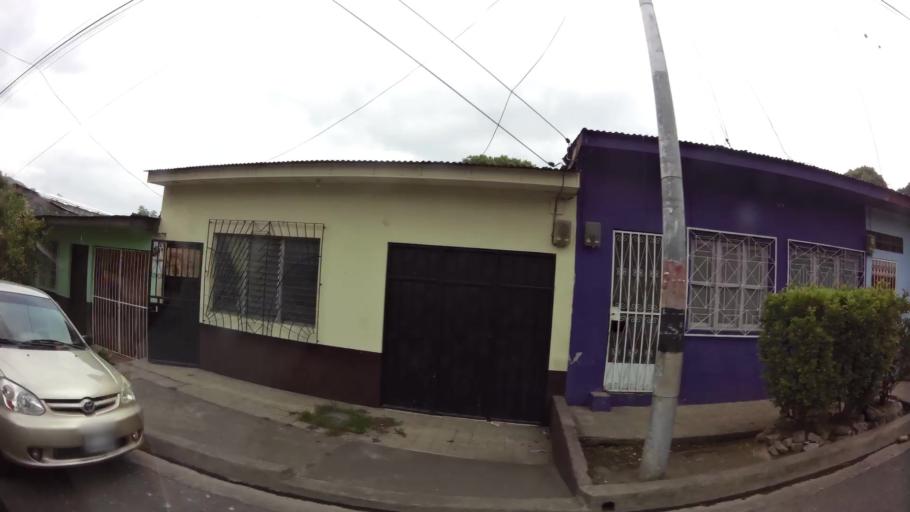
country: NI
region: Matagalpa
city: Matagalpa
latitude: 12.9233
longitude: -85.9162
